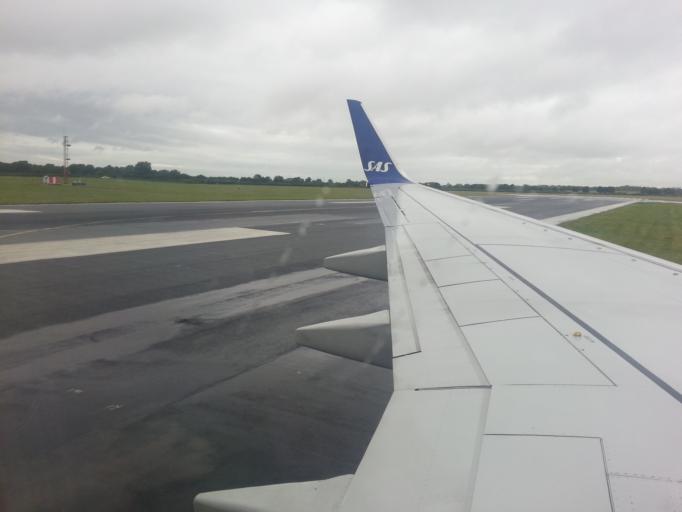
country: IE
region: Leinster
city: Ballymun
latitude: 53.4337
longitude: -6.2588
